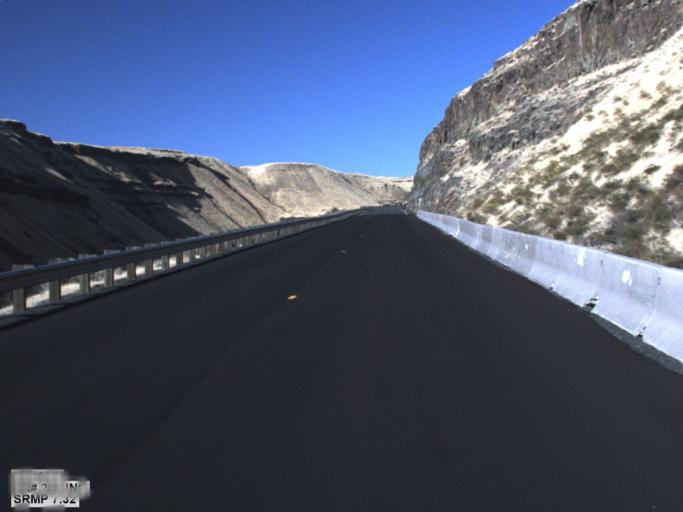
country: US
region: Washington
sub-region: Franklin County
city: Connell
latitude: 46.6194
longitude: -118.5578
